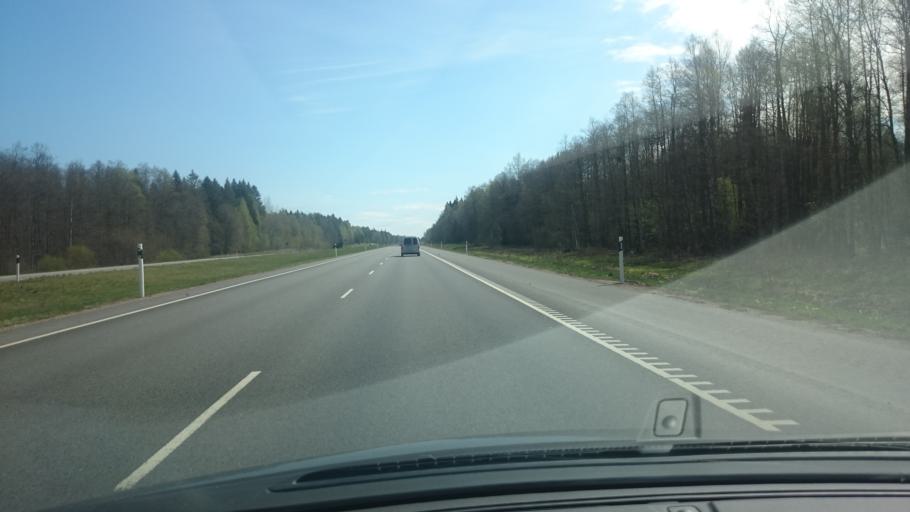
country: EE
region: Harju
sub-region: Loksa linn
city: Loksa
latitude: 59.4638
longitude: 25.7162
